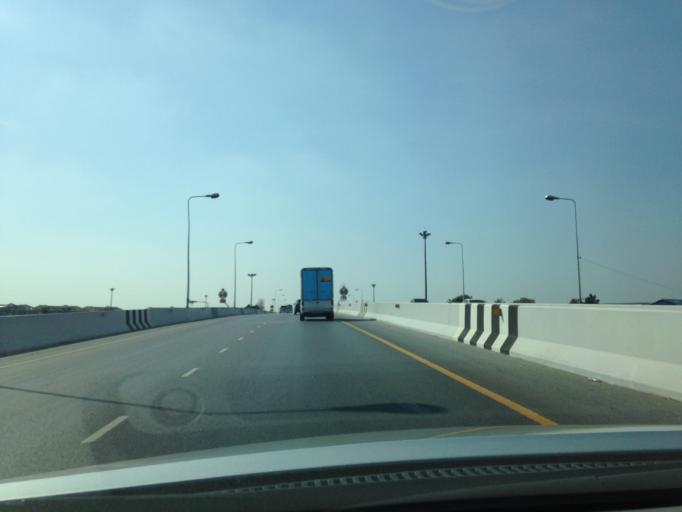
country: TH
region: Nonthaburi
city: Bang Yai
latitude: 13.8223
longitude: 100.4144
